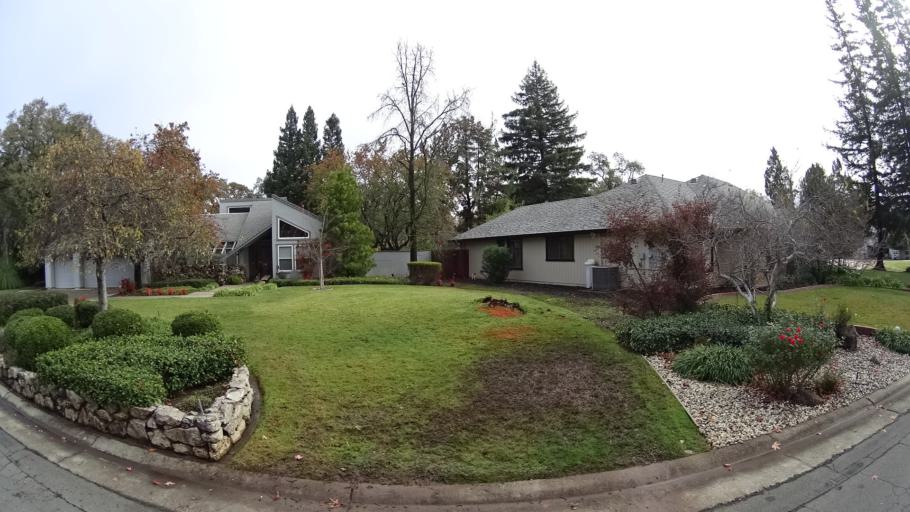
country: US
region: California
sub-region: Sacramento County
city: Antelope
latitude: 38.6838
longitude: -121.3210
